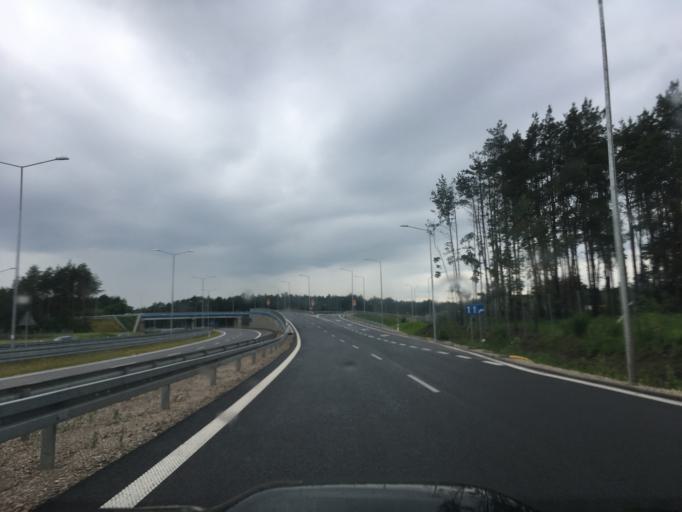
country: PL
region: Masovian Voivodeship
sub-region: Powiat piaseczynski
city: Gora Kalwaria
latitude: 51.9704
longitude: 21.1996
